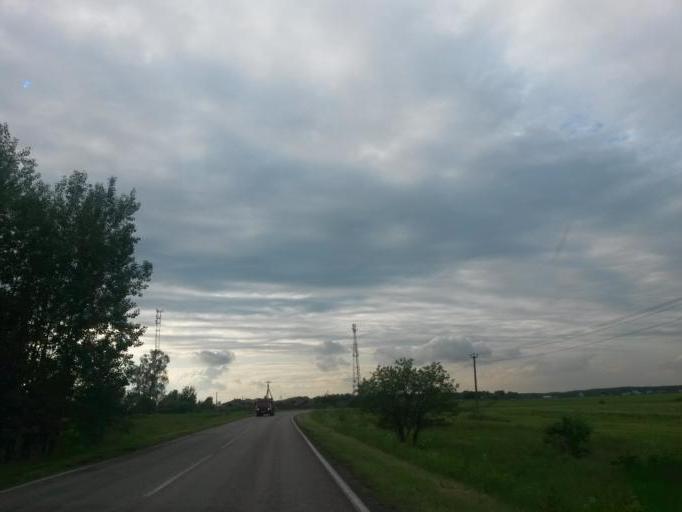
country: RU
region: Moskovskaya
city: Lyubuchany
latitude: 55.2331
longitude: 37.6457
